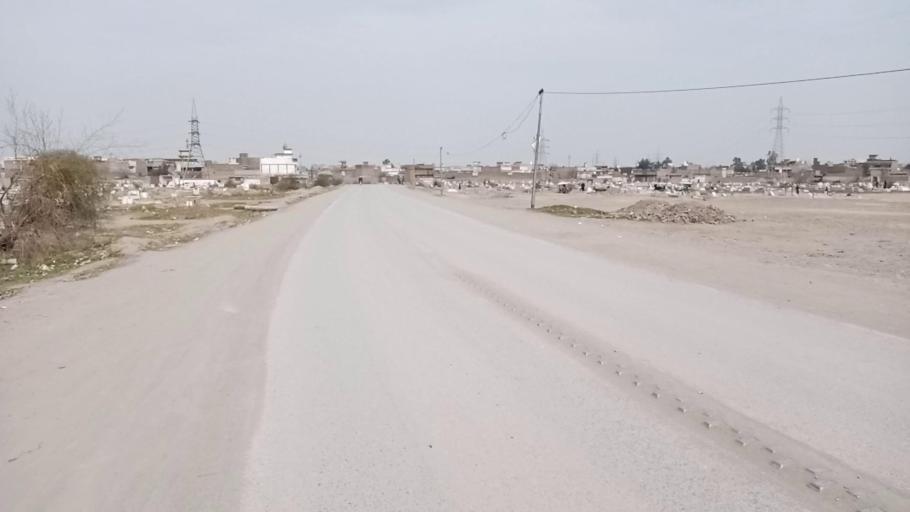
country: PK
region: Khyber Pakhtunkhwa
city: Peshawar
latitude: 33.9841
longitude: 71.4678
